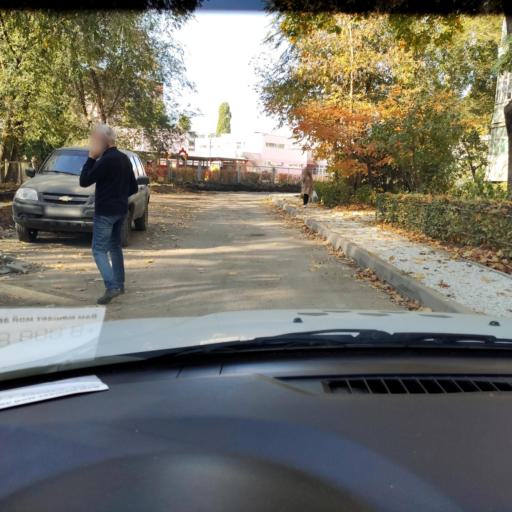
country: RU
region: Samara
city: Tol'yatti
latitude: 53.5189
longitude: 49.2649
